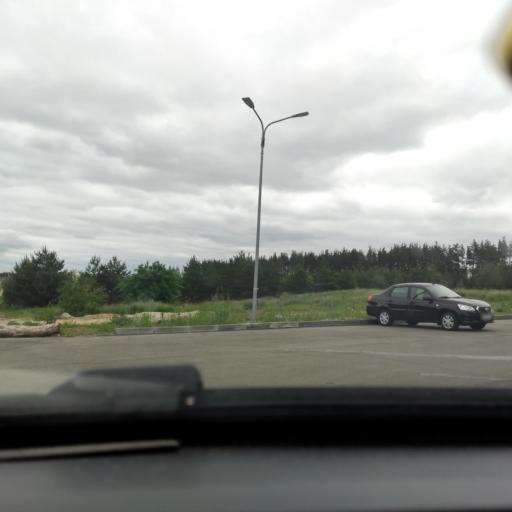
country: RU
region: Voronezj
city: Podgornoye
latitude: 51.8148
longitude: 39.1419
